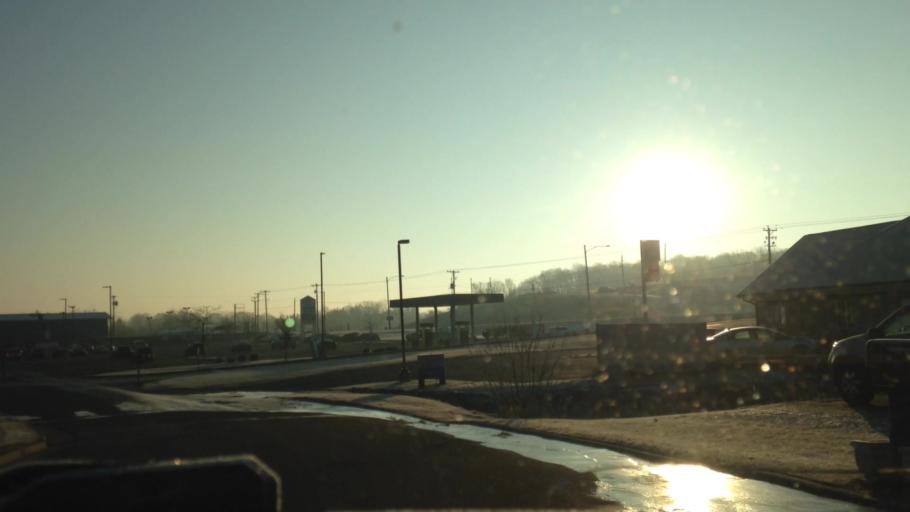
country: US
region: Wisconsin
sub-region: Dodge County
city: Mayville
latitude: 43.4955
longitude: -88.5657
